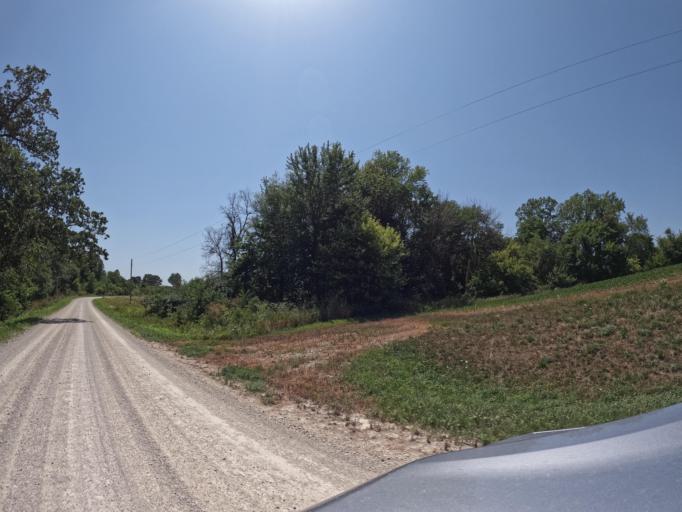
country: US
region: Iowa
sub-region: Henry County
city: Mount Pleasant
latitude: 40.9469
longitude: -91.6515
